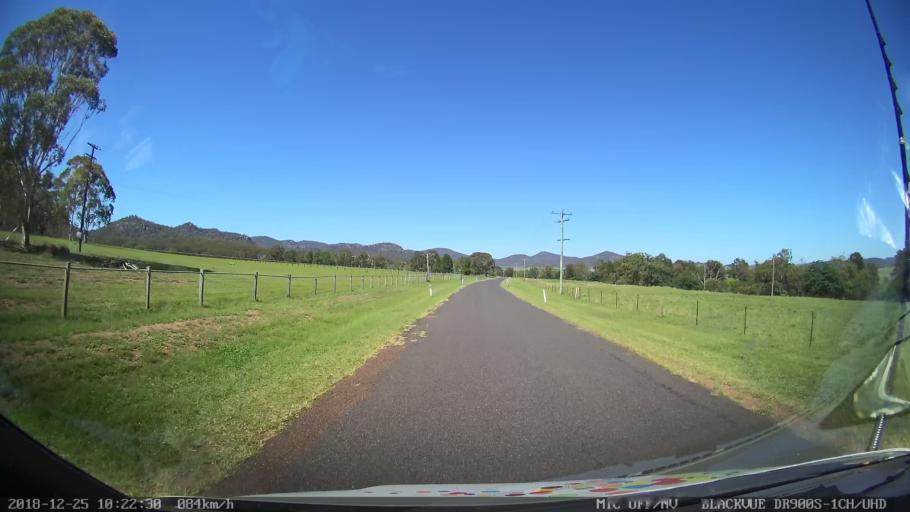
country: AU
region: New South Wales
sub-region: Muswellbrook
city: Denman
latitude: -32.3770
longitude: 150.5317
